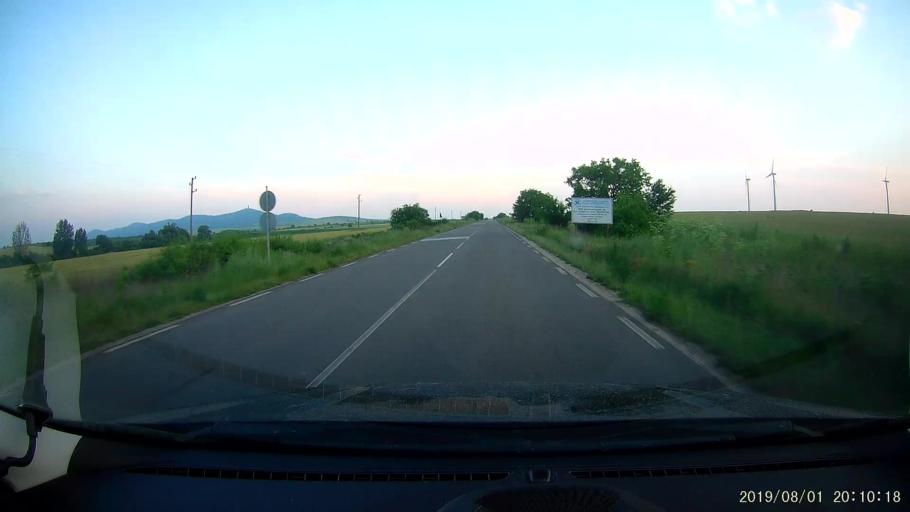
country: BG
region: Yambol
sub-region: Obshtina Yambol
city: Yambol
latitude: 42.4839
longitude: 26.5981
